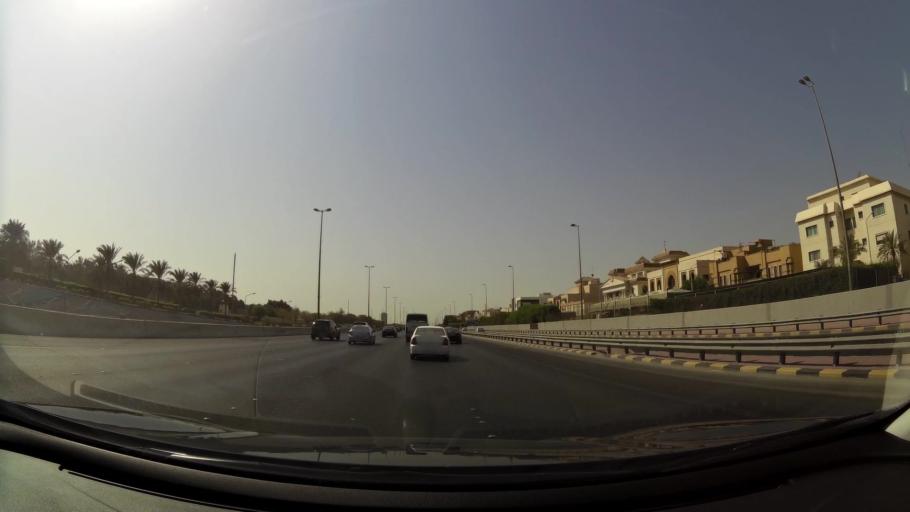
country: KW
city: Bayan
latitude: 29.3096
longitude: 48.0362
